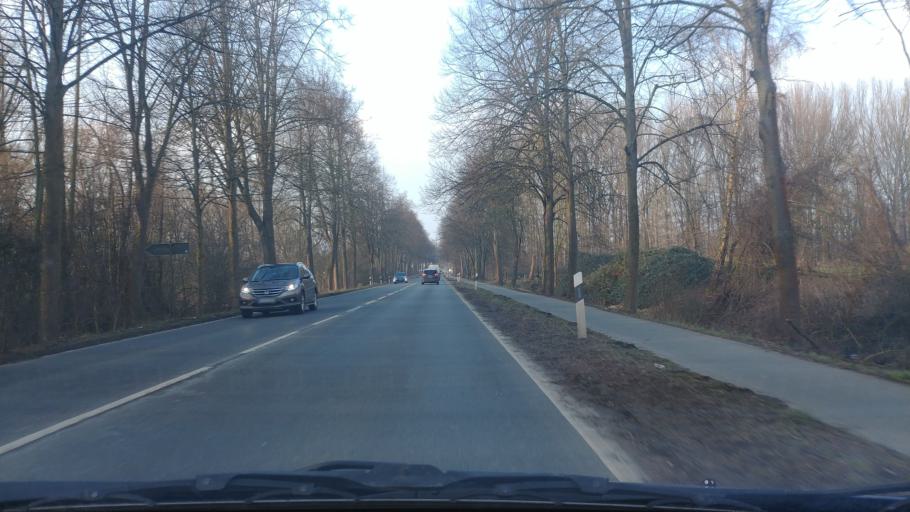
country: DE
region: Lower Saxony
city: Hemmingen
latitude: 52.3109
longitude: 9.7328
